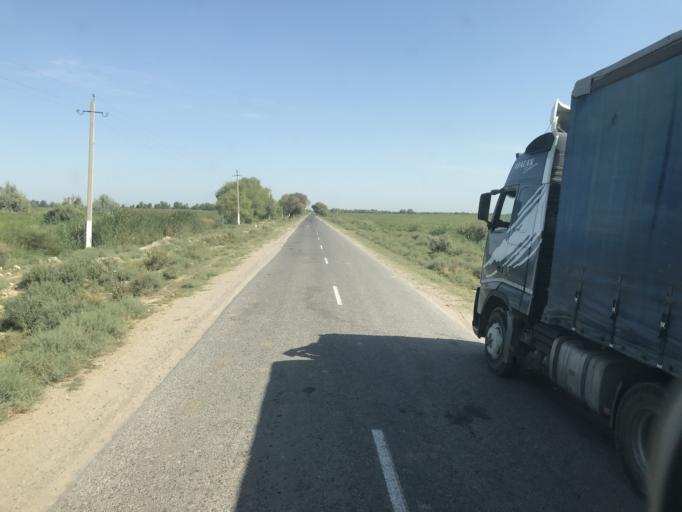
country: KZ
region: Ongtustik Qazaqstan
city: Myrzakent
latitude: 40.6694
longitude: 68.6333
